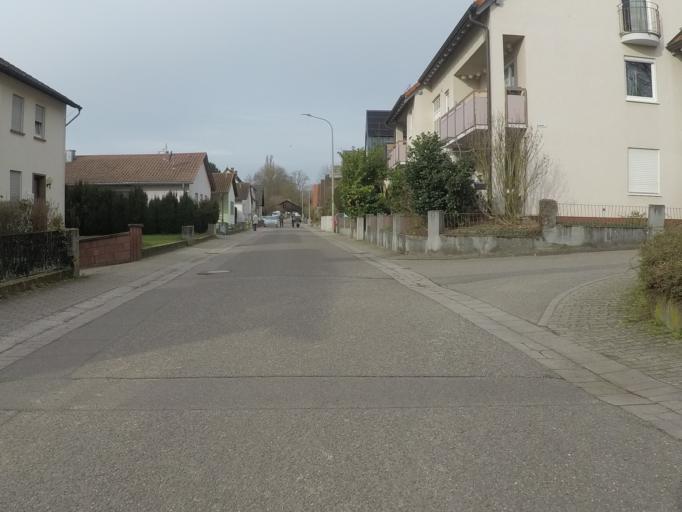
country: DE
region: Rheinland-Pfalz
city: Billigheim-Ingenheim
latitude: 49.1386
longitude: 8.0794
